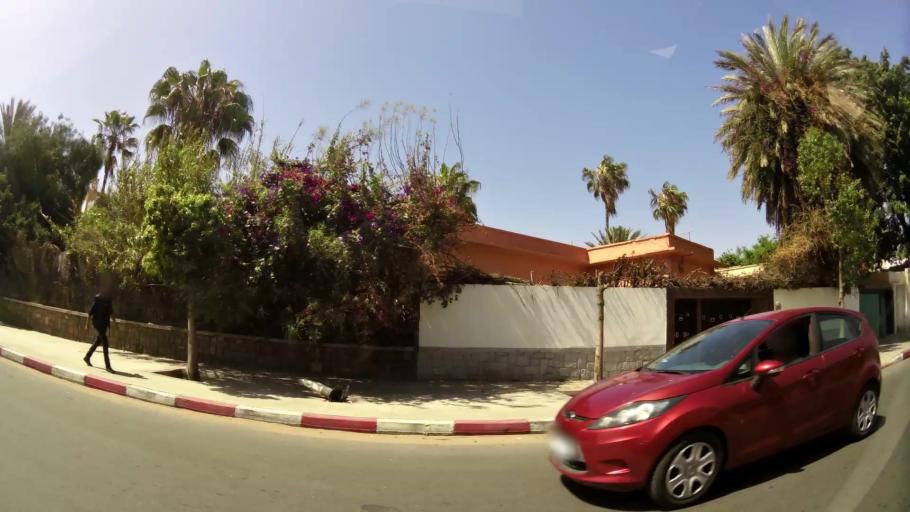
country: MA
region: Souss-Massa-Draa
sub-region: Agadir-Ida-ou-Tnan
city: Agadir
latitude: 30.4132
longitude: -9.5883
